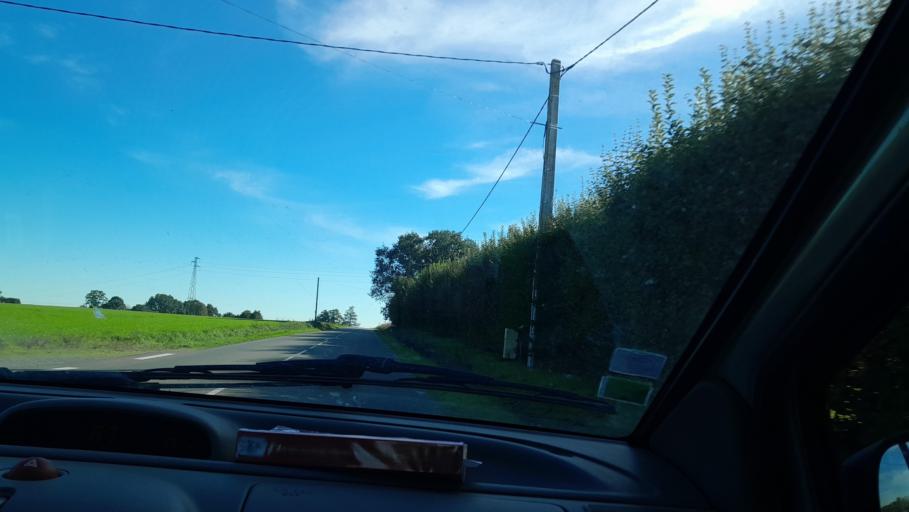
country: FR
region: Brittany
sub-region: Departement d'Ille-et-Vilaine
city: Argentre-du-Plessis
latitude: 48.0370
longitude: -1.1434
